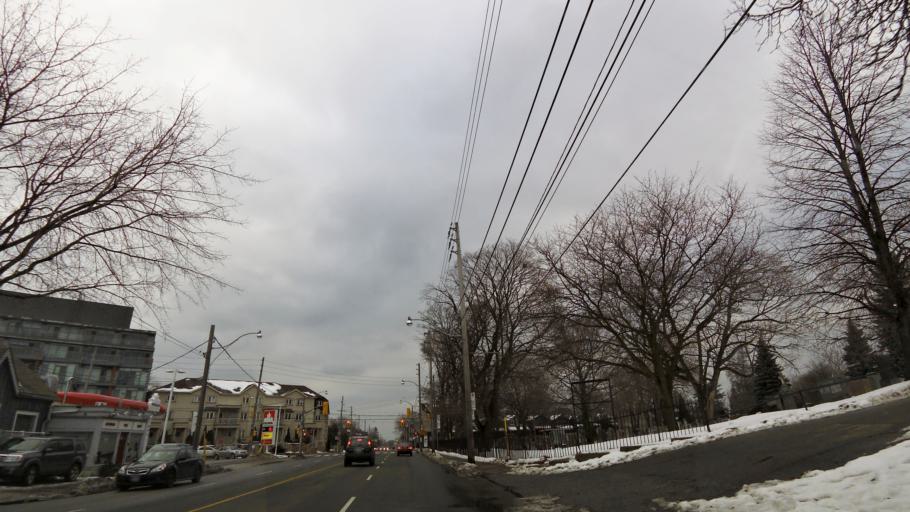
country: CA
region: Ontario
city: Scarborough
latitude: 43.6748
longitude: -79.3083
